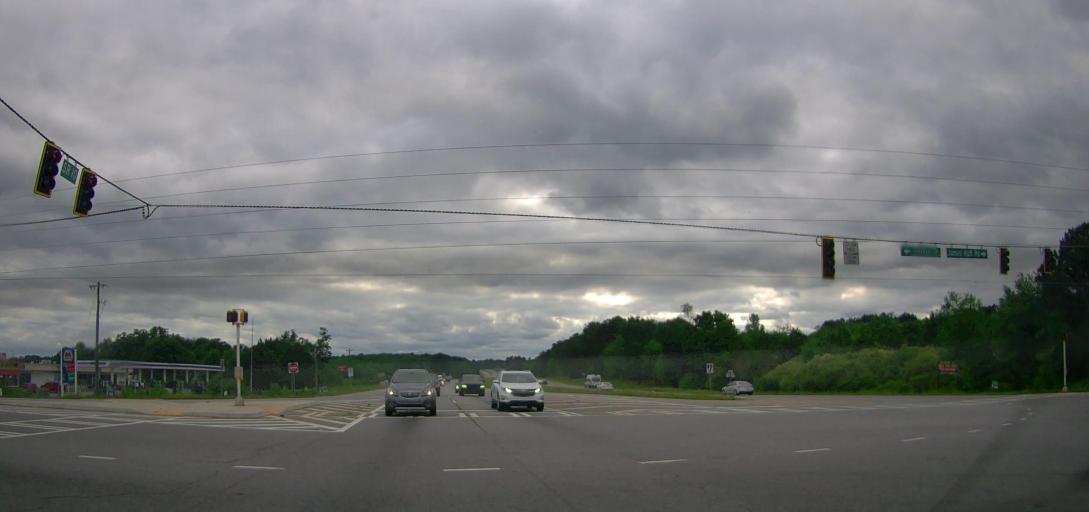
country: US
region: Georgia
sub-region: Walton County
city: Monroe
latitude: 33.8142
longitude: -83.6799
